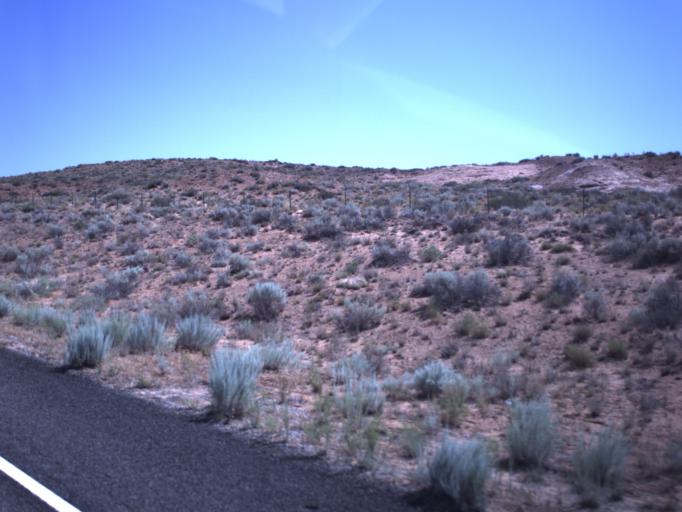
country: US
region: Utah
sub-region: Emery County
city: Ferron
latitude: 38.5554
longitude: -110.6142
